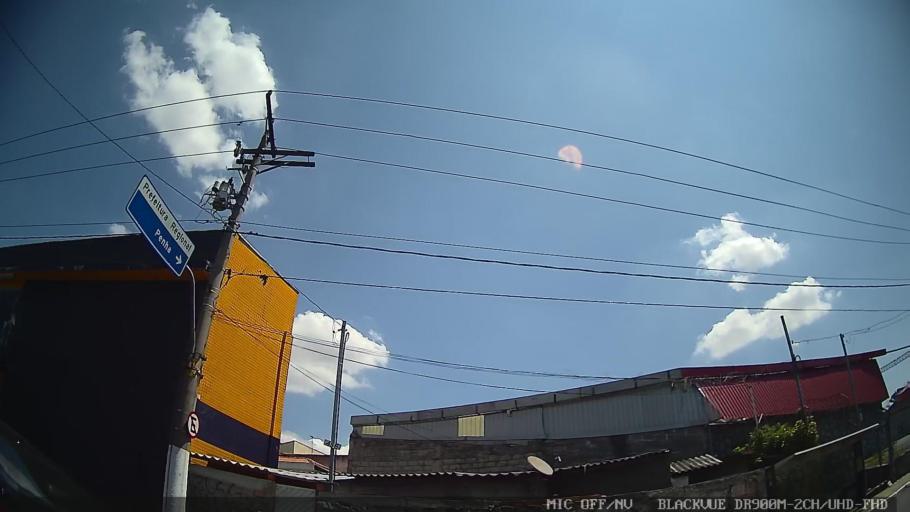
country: BR
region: Sao Paulo
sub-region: Guarulhos
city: Guarulhos
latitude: -23.5171
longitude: -46.5162
